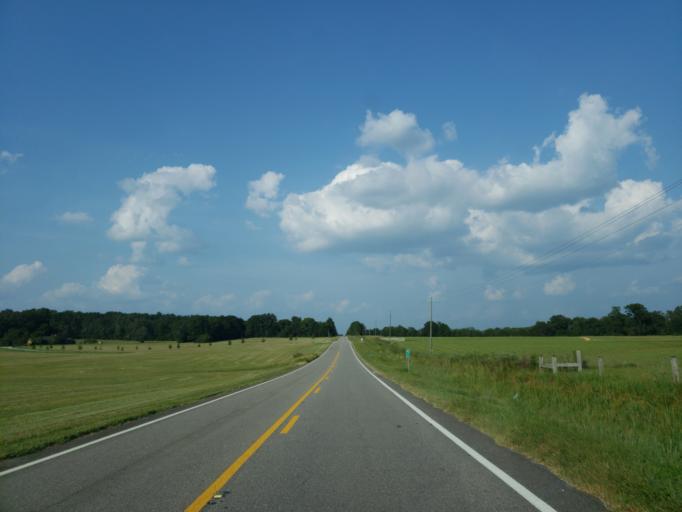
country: US
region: Alabama
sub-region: Greene County
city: Eutaw
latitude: 32.7619
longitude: -88.0080
